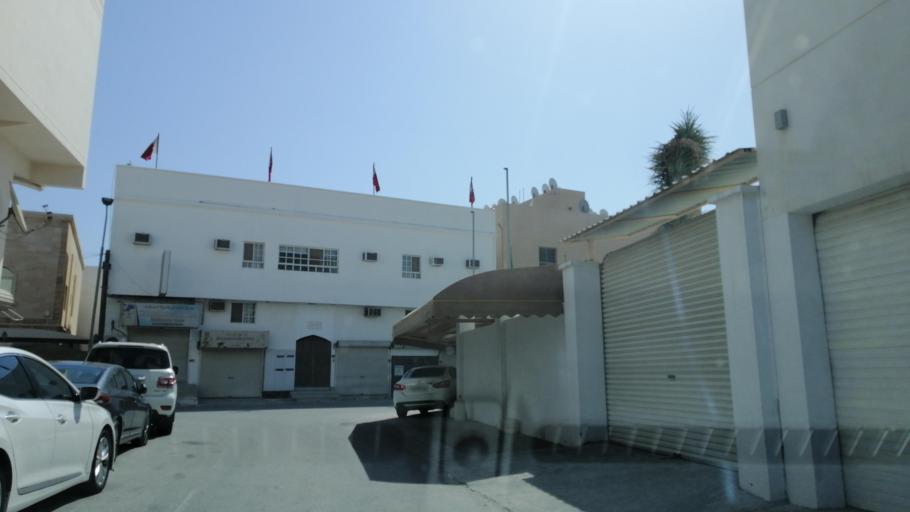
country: BH
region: Muharraq
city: Al Hadd
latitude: 26.2464
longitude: 50.6354
